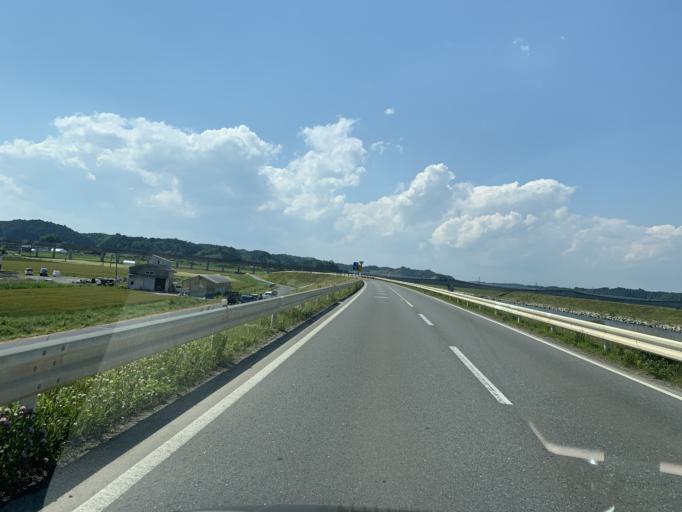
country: JP
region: Miyagi
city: Yamoto
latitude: 38.3855
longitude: 141.1662
